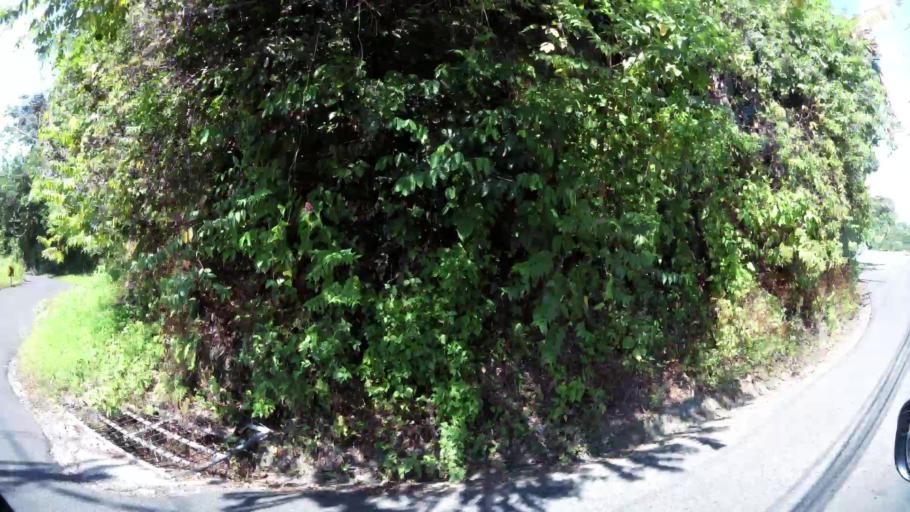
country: CR
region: Puntarenas
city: Quepos
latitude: 9.4015
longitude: -84.1605
